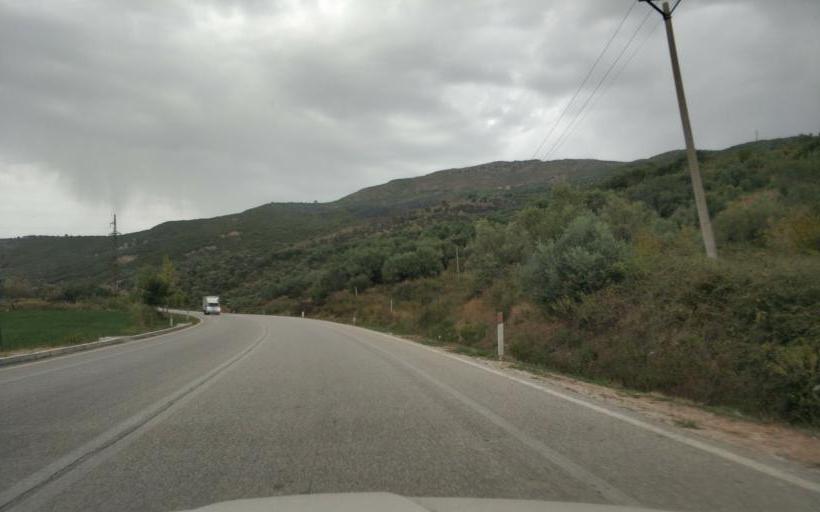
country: AL
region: Fier
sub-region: Rrethi i Mallakastres
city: Hekal
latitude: 40.5195
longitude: 19.7419
